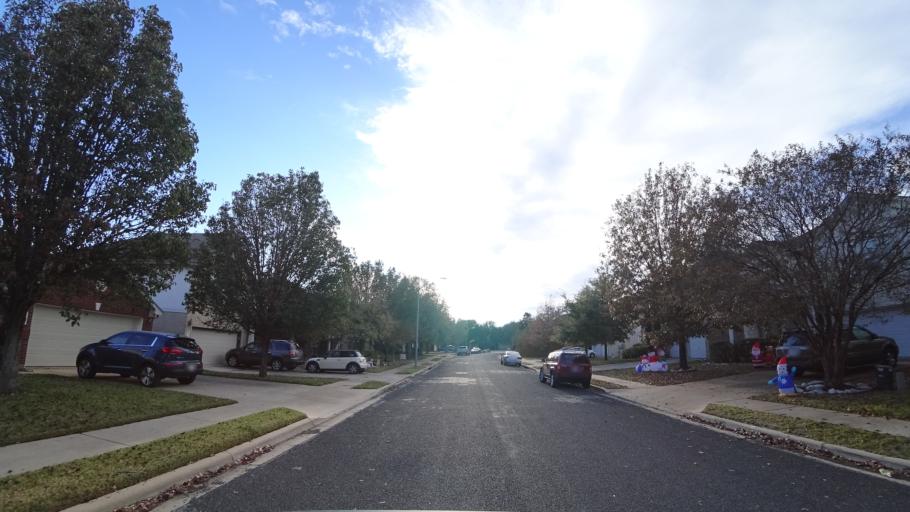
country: US
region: Texas
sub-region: Williamson County
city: Brushy Creek
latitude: 30.5003
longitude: -97.7389
